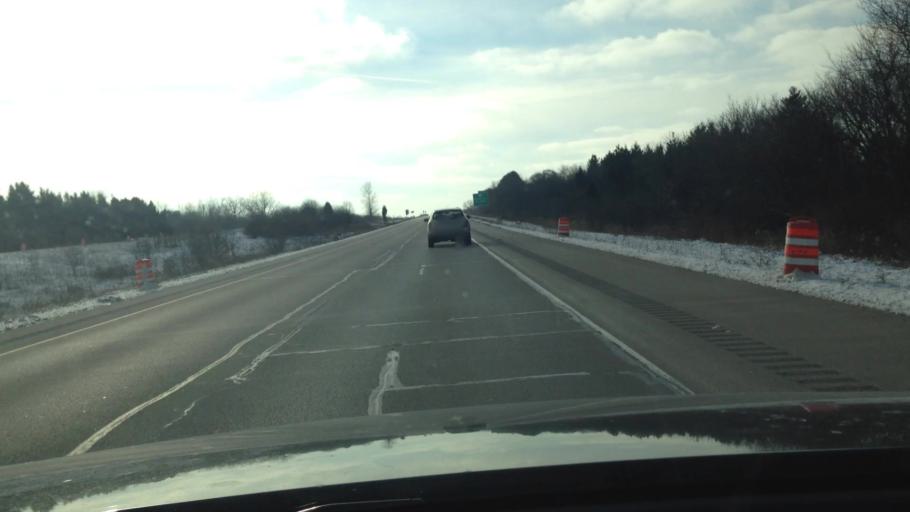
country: US
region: Wisconsin
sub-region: Waukesha County
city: Big Bend
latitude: 42.9227
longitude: -88.1931
